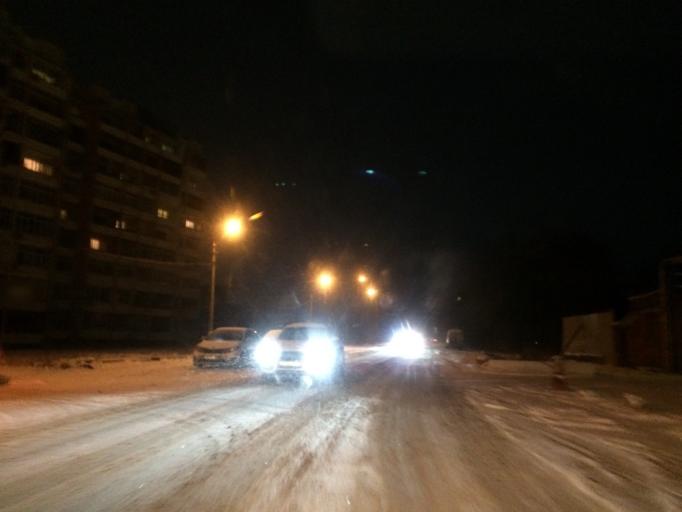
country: RU
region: Tula
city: Mendeleyevskiy
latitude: 54.1574
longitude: 37.6084
